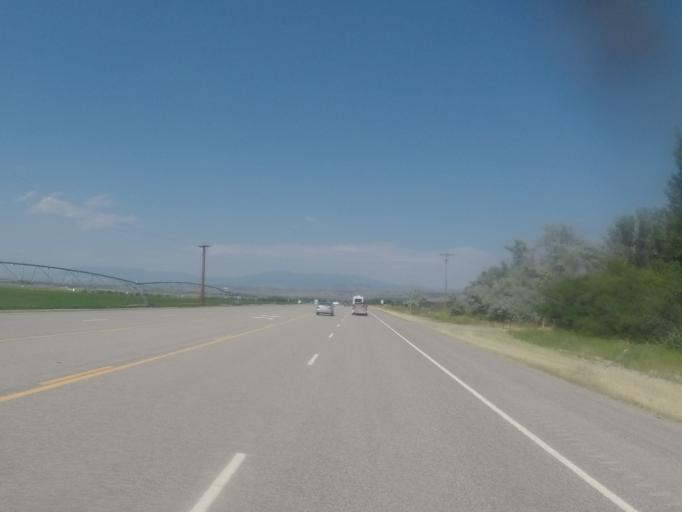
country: US
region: Montana
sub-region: Broadwater County
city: Townsend
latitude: 46.1416
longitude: -111.4765
